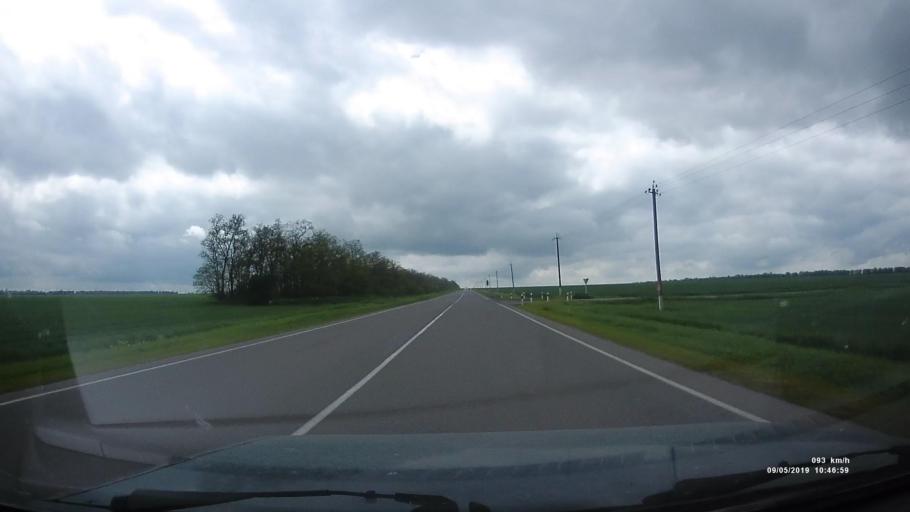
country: RU
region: Rostov
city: Peshkovo
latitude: 46.9770
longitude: 39.3557
